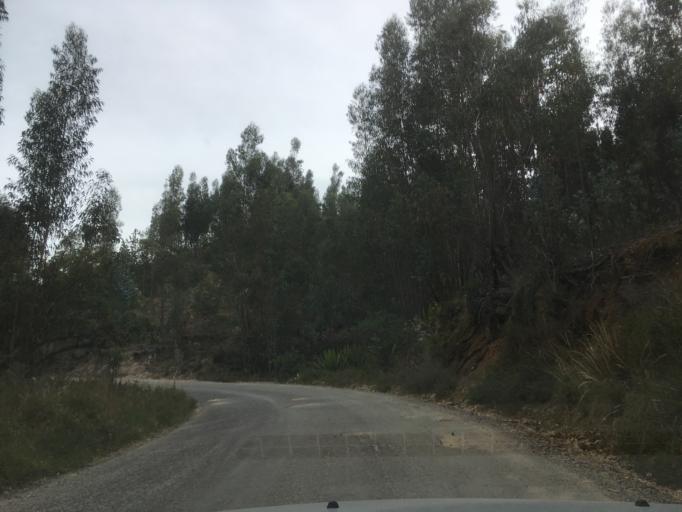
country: CO
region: Boyaca
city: Firavitoba
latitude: 5.6776
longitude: -73.0146
